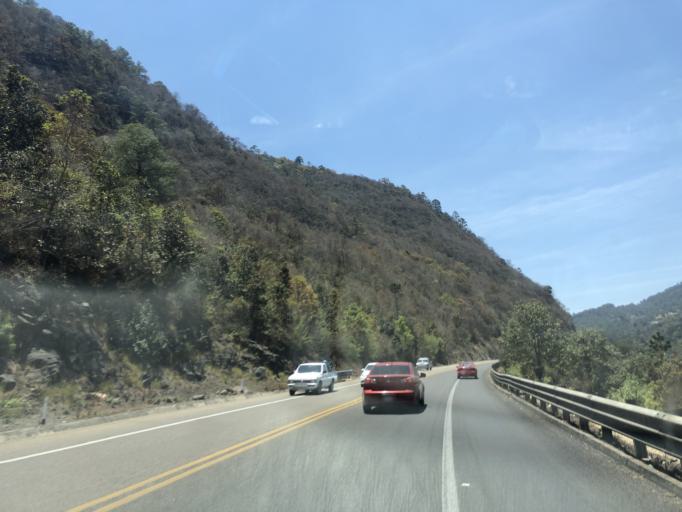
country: MX
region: Chiapas
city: San Cristobal de las Casas
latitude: 16.7196
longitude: -92.6673
